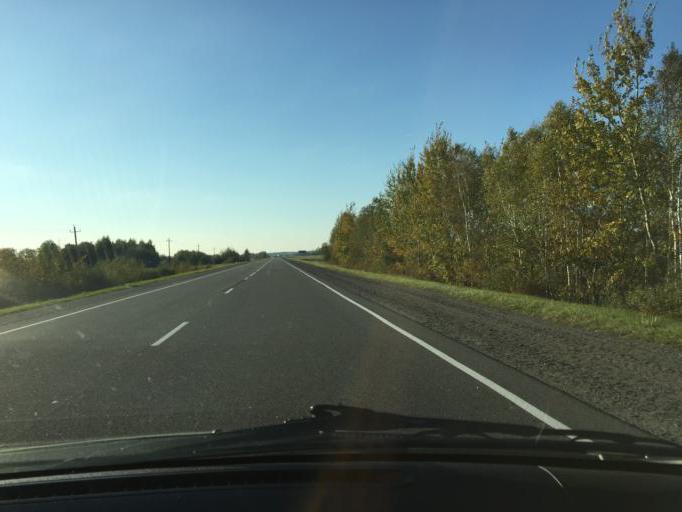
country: BY
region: Brest
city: Horad Luninyets
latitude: 52.3132
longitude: 26.6550
